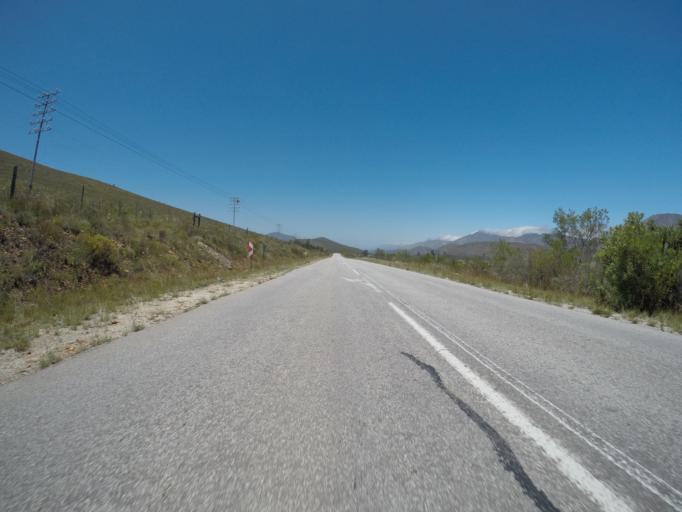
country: ZA
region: Eastern Cape
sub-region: Cacadu District Municipality
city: Kareedouw
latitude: -33.8501
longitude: 23.9729
